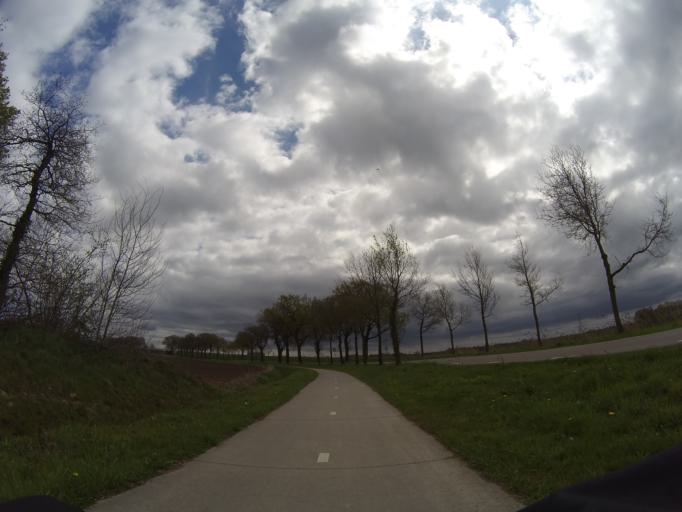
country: NL
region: Drenthe
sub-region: Gemeente Coevorden
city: Sleen
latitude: 52.7847
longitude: 6.8412
